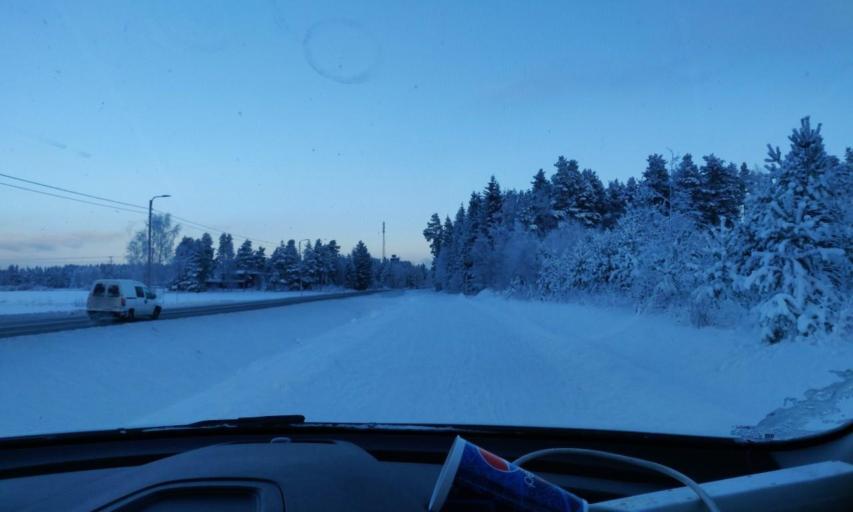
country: FI
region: Northern Ostrobothnia
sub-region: Ylivieska
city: Ylivieska
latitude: 64.0648
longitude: 24.4959
